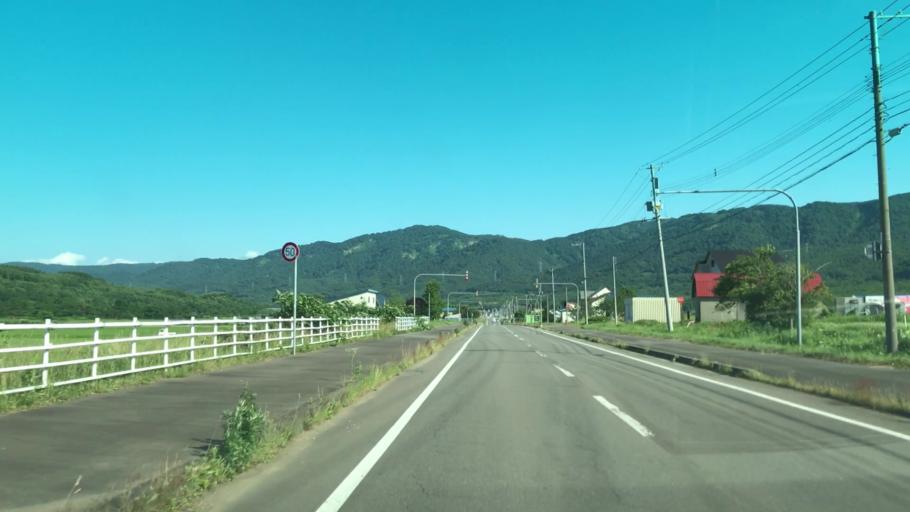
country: JP
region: Hokkaido
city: Yoichi
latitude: 43.0521
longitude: 140.7211
